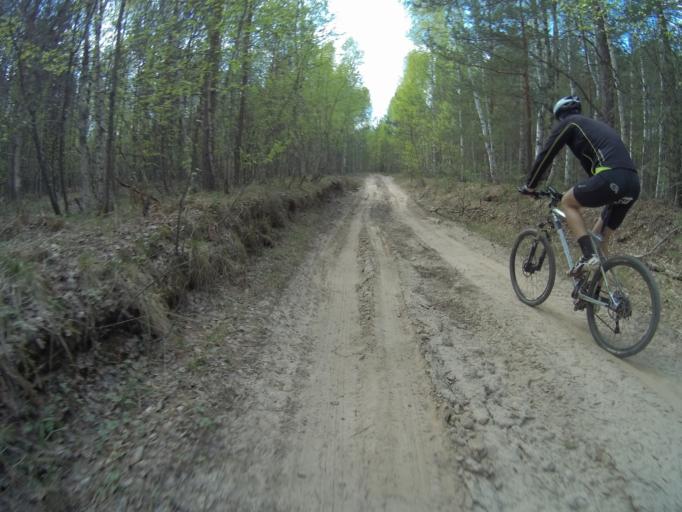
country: RU
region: Vladimir
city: Raduzhnyy
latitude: 55.9639
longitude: 40.2036
